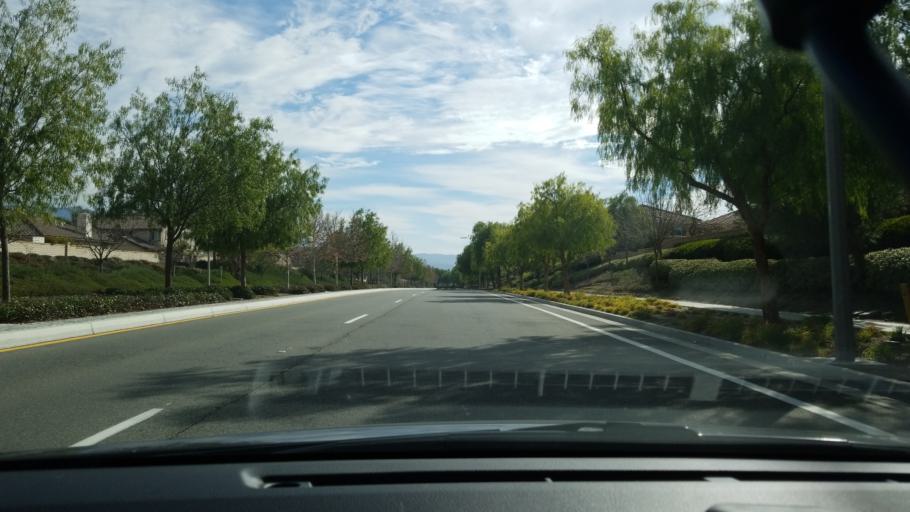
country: US
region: California
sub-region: Riverside County
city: Temecula
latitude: 33.5013
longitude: -117.0889
